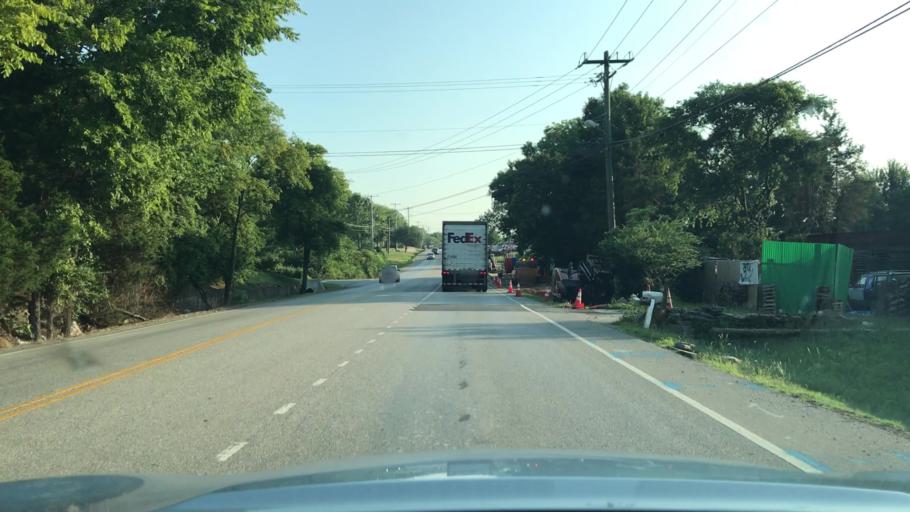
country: US
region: Tennessee
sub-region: Rutherford County
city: La Vergne
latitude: 36.0319
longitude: -86.6121
